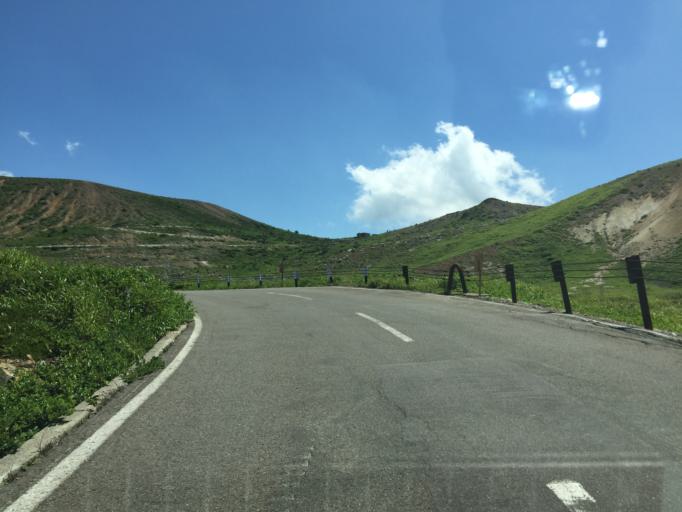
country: JP
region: Fukushima
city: Fukushima-shi
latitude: 37.7308
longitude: 140.2587
